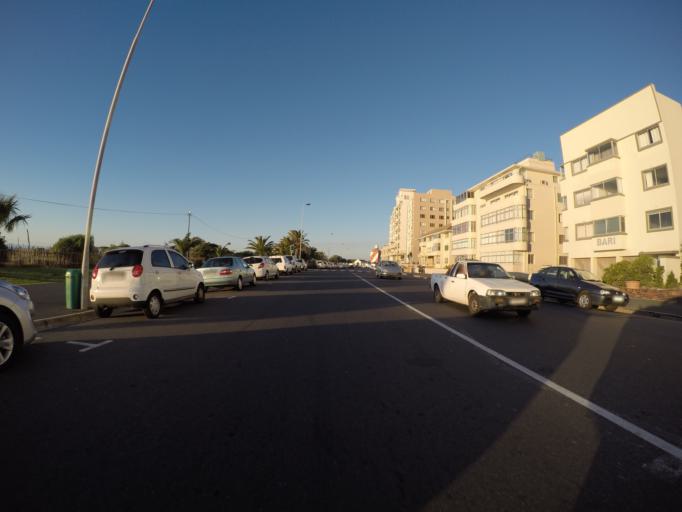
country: ZA
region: Western Cape
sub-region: City of Cape Town
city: Cape Town
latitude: -33.9036
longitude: 18.3988
